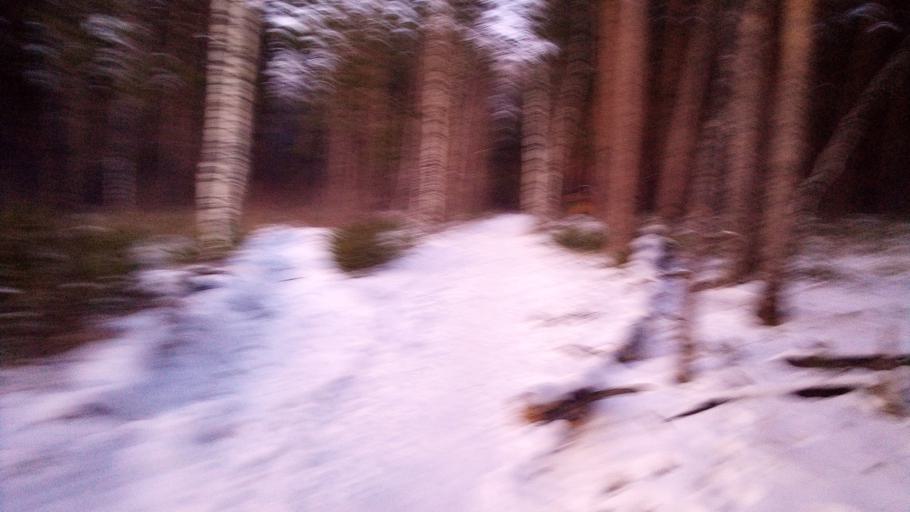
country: RU
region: Chelyabinsk
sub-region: Gorod Chelyabinsk
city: Chelyabinsk
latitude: 55.1649
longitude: 61.3316
